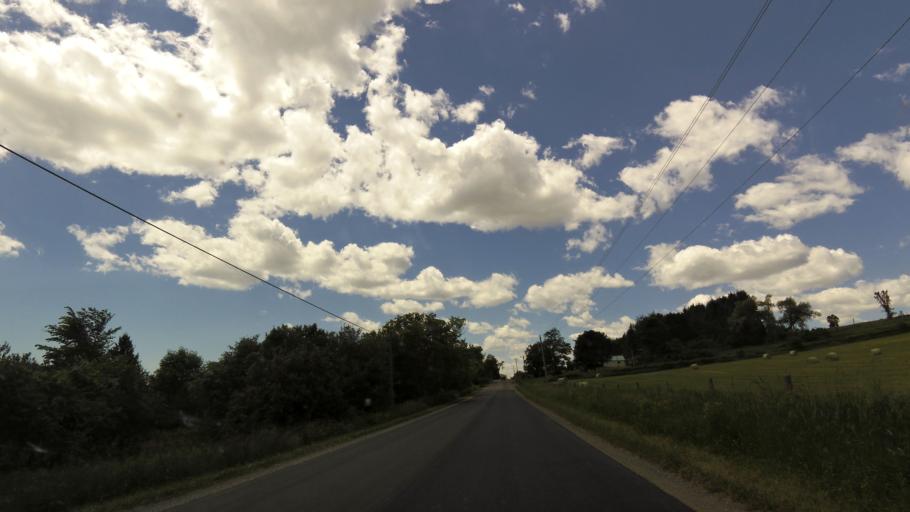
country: CA
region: Ontario
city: Oshawa
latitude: 43.9682
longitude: -78.5357
